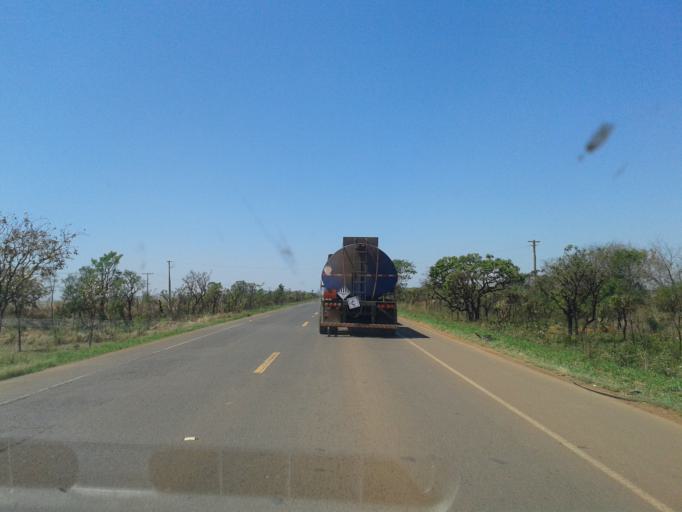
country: BR
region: Minas Gerais
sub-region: Araxa
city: Araxa
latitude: -19.3164
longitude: -47.3874
